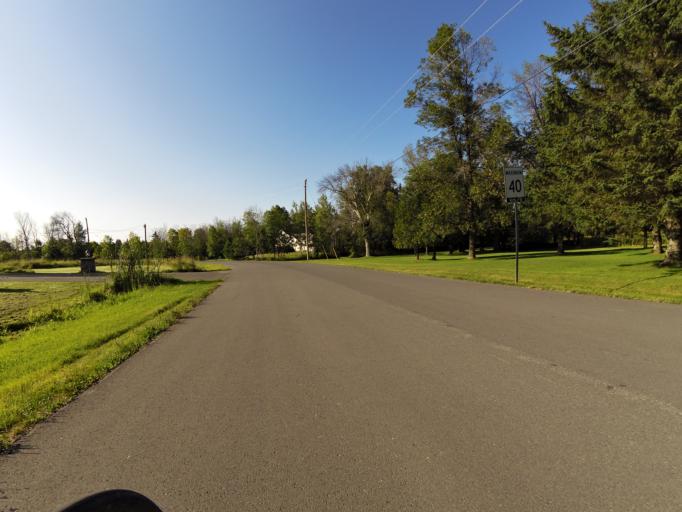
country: CA
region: Ontario
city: Bells Corners
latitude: 45.4769
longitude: -76.0319
